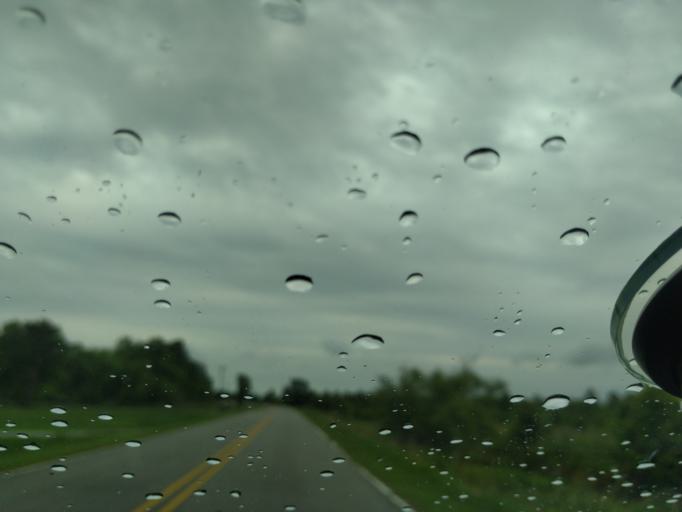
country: US
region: North Carolina
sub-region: Beaufort County
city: Belhaven
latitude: 35.7550
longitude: -76.5150
